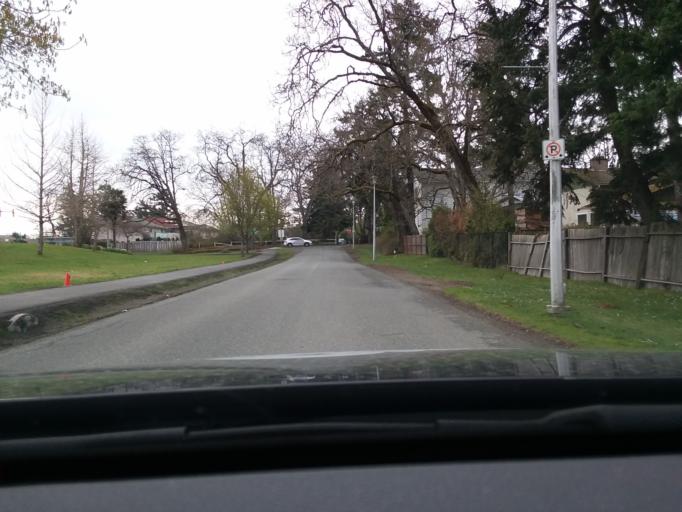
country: CA
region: British Columbia
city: Oak Bay
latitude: 48.4768
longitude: -123.3284
